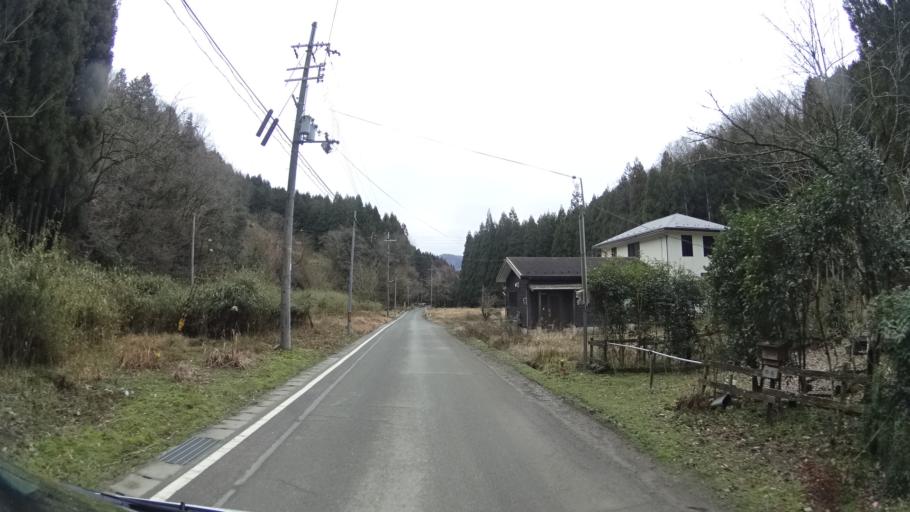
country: JP
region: Kyoto
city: Maizuru
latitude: 35.3480
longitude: 135.3490
